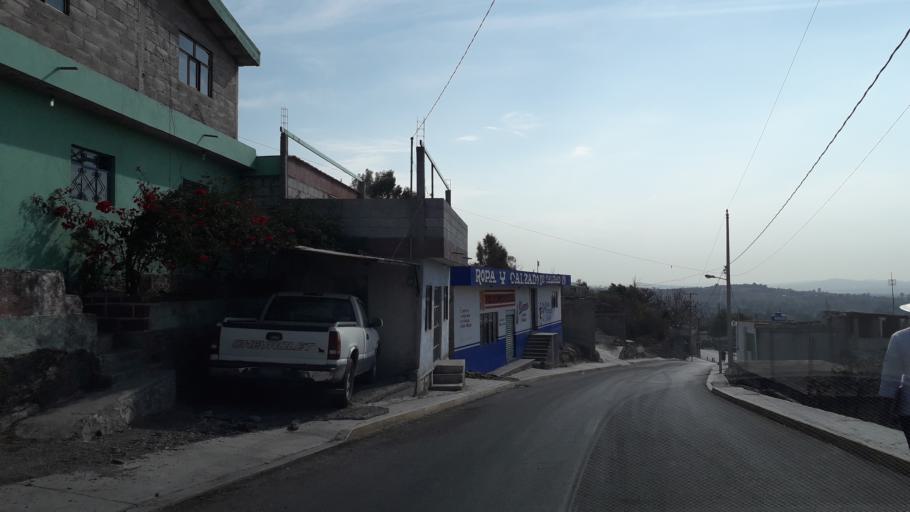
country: MX
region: Puebla
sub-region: Puebla
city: San Andres Azumiatla
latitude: 18.9051
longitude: -98.2511
